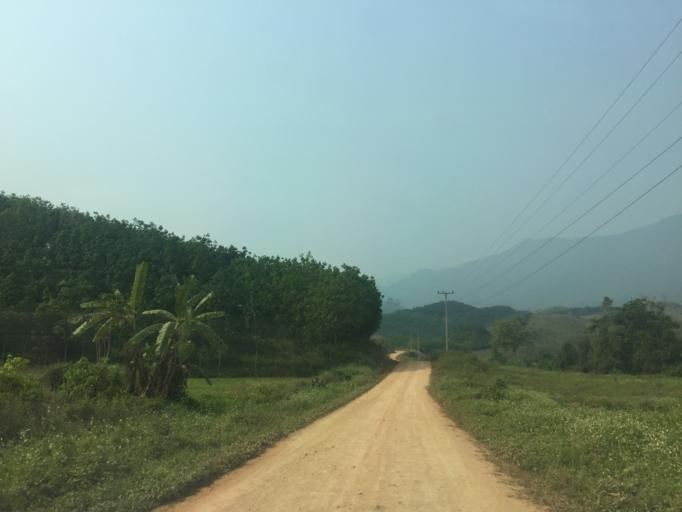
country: TH
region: Phayao
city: Phu Sang
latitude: 19.6459
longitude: 100.5255
